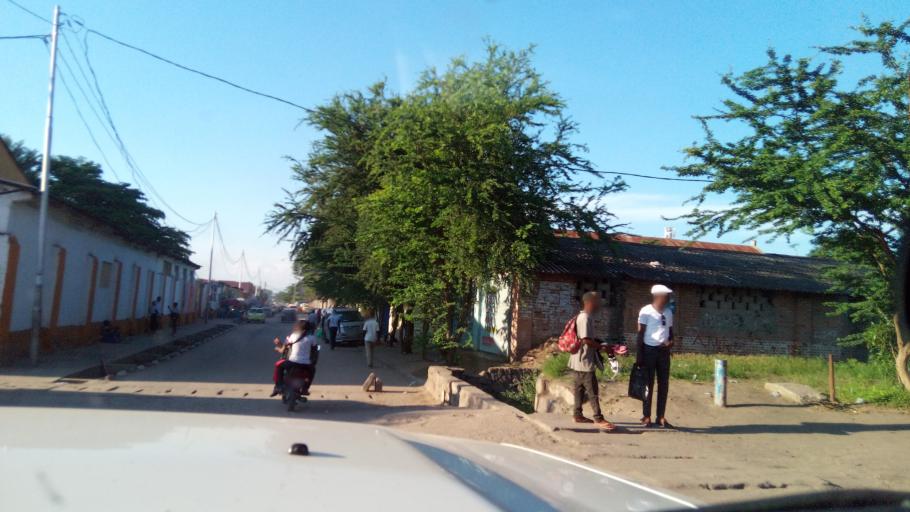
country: CD
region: Kinshasa
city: Kinshasa
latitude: -4.3397
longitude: 15.2670
